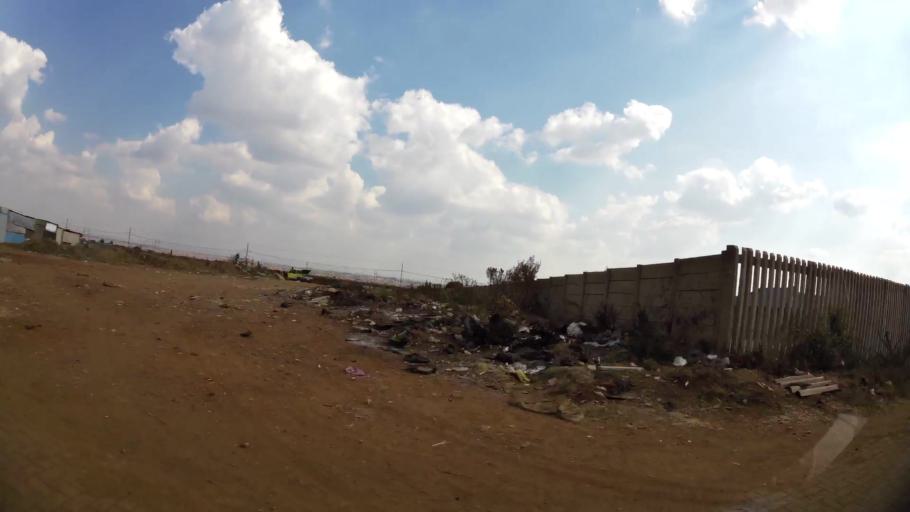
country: ZA
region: Gauteng
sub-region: Ekurhuleni Metropolitan Municipality
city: Springs
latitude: -26.1263
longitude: 28.4730
